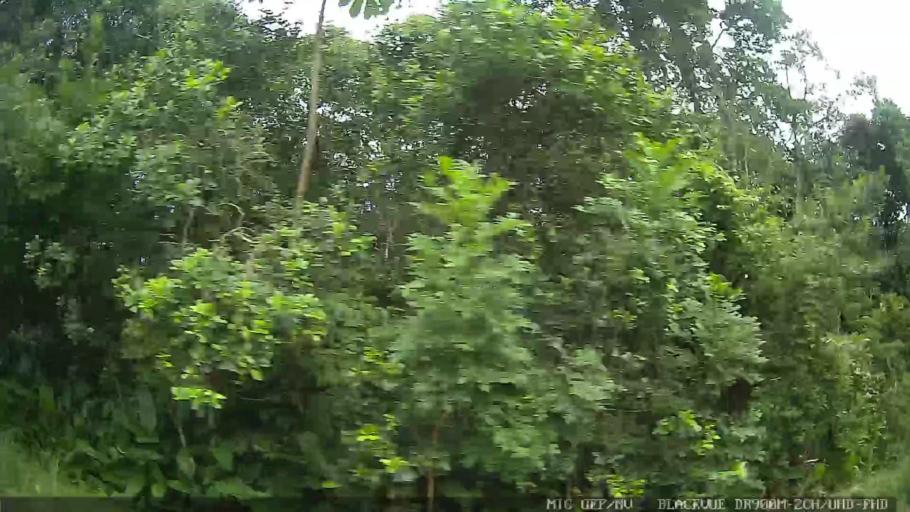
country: BR
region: Sao Paulo
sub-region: Iguape
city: Iguape
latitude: -24.6527
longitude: -47.4028
